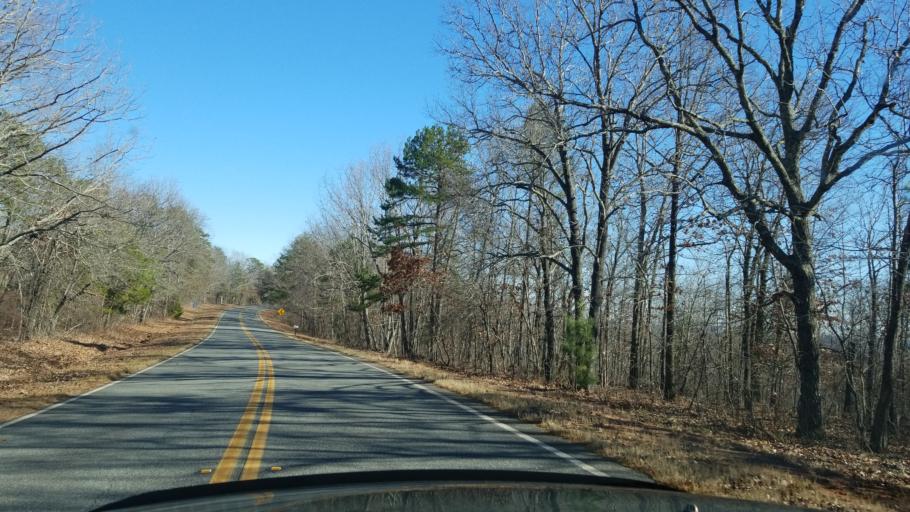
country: US
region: Georgia
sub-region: Talbot County
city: Sardis
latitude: 32.8435
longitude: -84.6906
